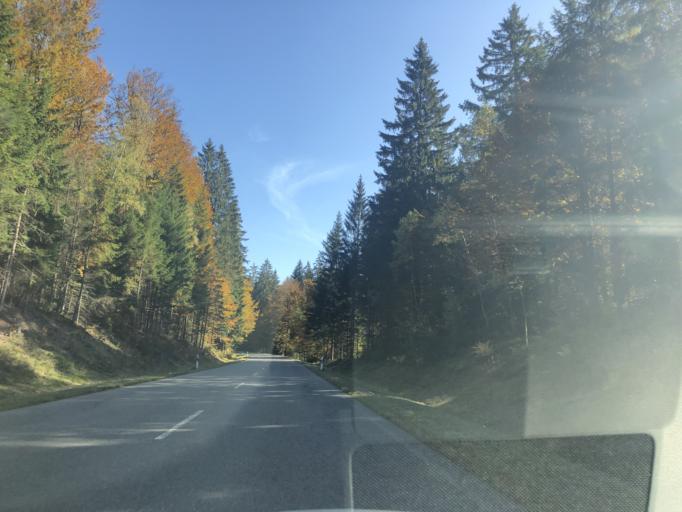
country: DE
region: Bavaria
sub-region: Lower Bavaria
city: Neuschonau
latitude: 48.9154
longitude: 13.4575
